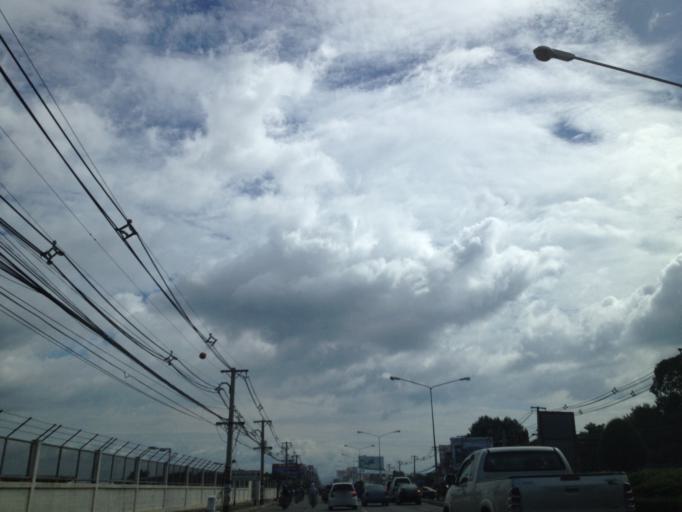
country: TH
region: Chiang Mai
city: Chiang Mai
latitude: 18.7486
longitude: 98.9629
